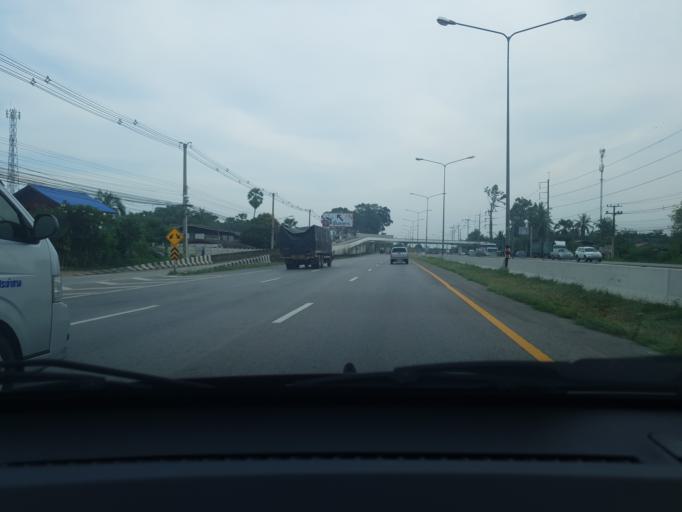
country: TH
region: Phetchaburi
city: Phetchaburi
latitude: 13.1464
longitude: 99.8554
